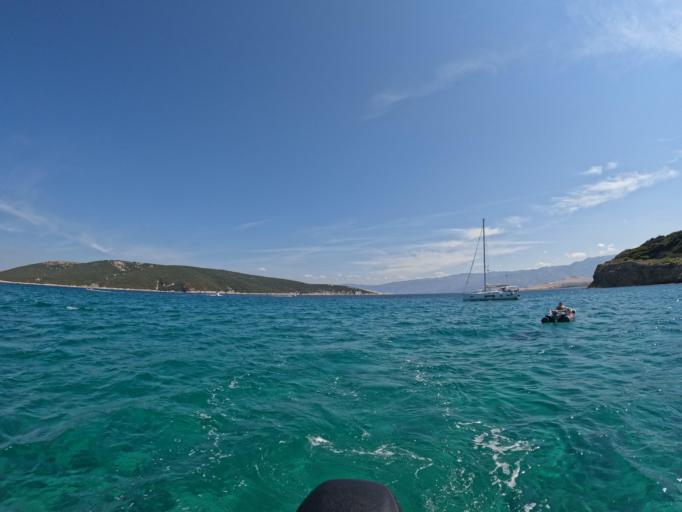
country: HR
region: Primorsko-Goranska
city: Lopar
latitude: 44.8428
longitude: 14.7547
